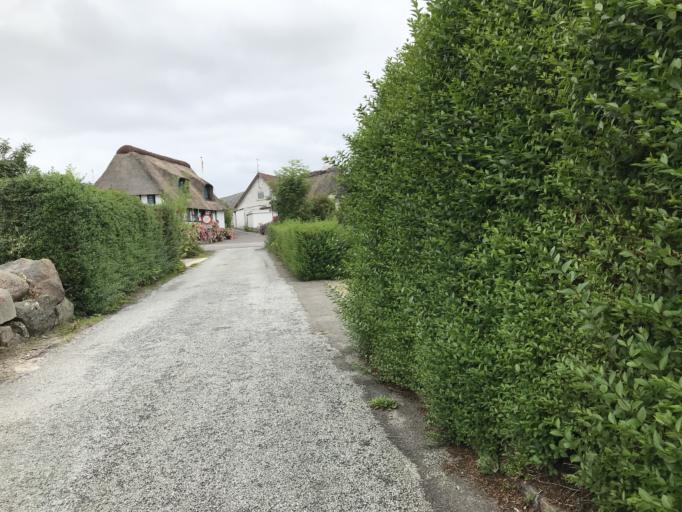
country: DK
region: South Denmark
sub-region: Faaborg-Midtfyn Kommune
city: Faaborg
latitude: 54.9405
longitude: 10.2566
